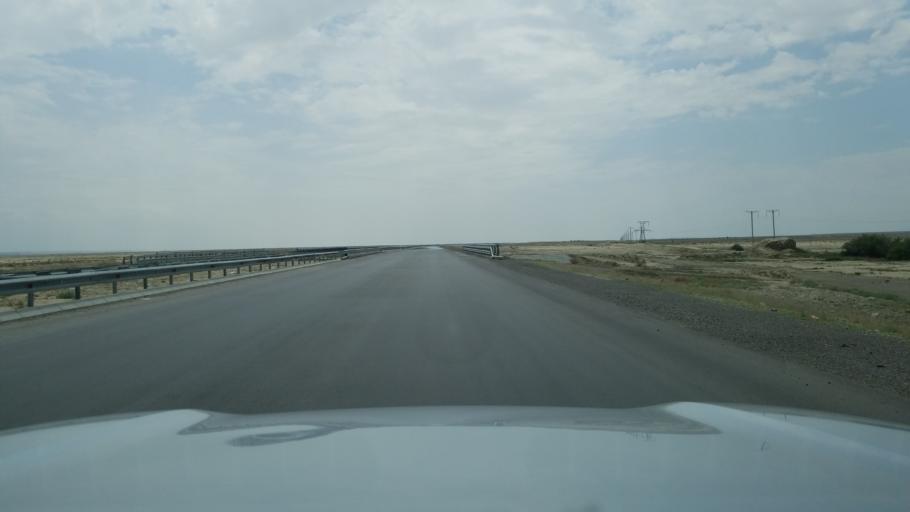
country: TM
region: Balkan
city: Gazanjyk
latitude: 39.2311
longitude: 55.0725
